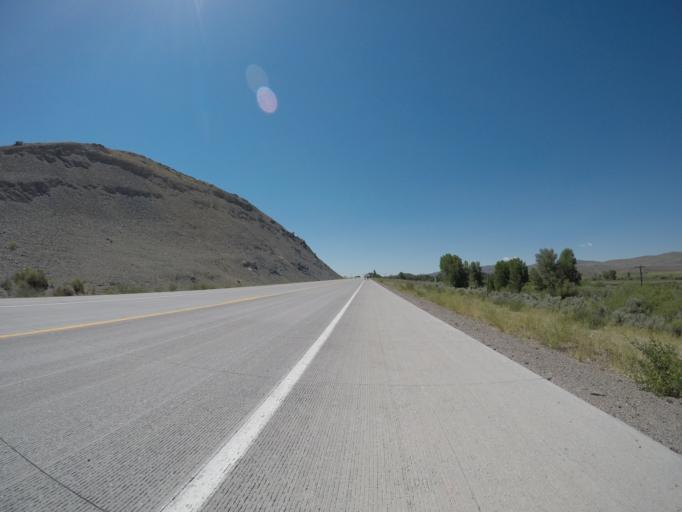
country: US
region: Idaho
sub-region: Bear Lake County
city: Montpelier
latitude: 42.1279
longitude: -110.9684
